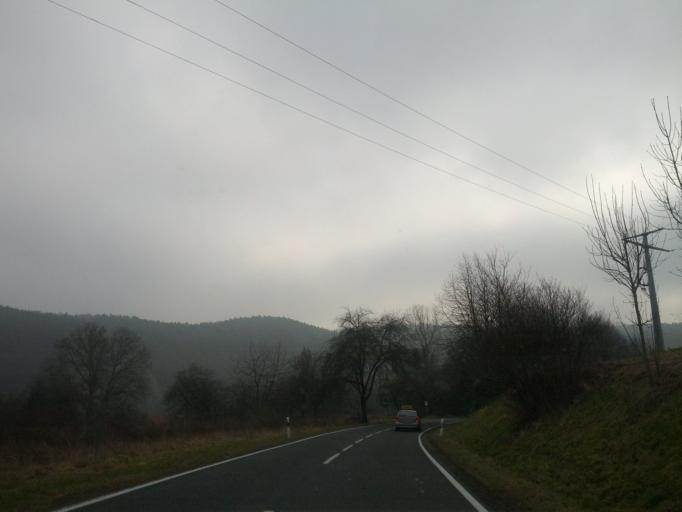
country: DE
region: Thuringia
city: Creuzburg
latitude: 51.0637
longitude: 10.2702
